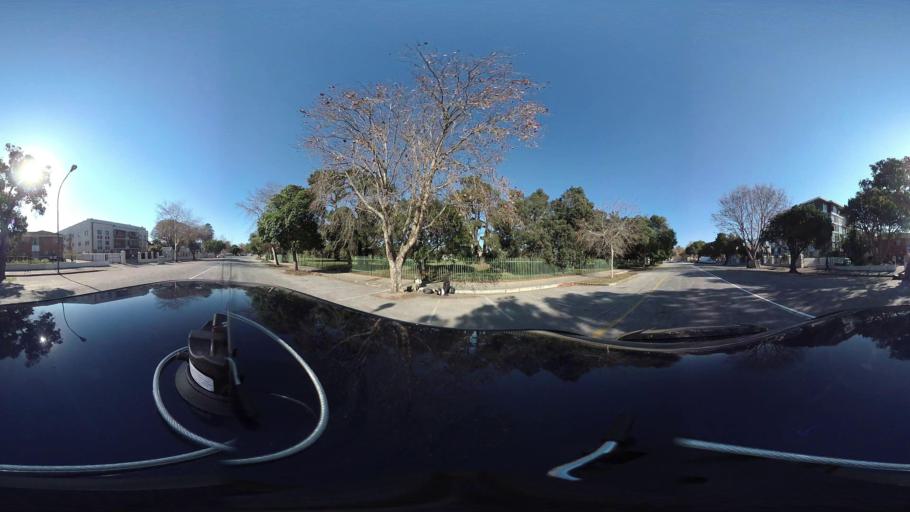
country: ZA
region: Eastern Cape
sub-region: Nelson Mandela Bay Metropolitan Municipality
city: Port Elizabeth
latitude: -33.9634
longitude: 25.6107
